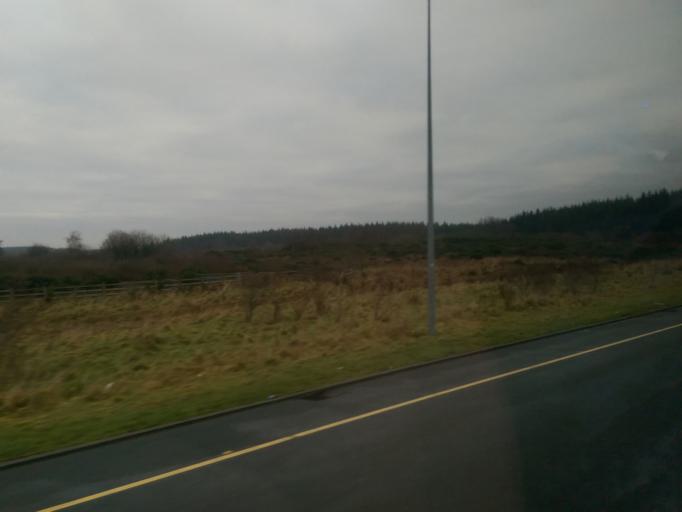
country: IE
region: Connaught
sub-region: County Galway
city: Loughrea
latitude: 53.2827
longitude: -8.4118
